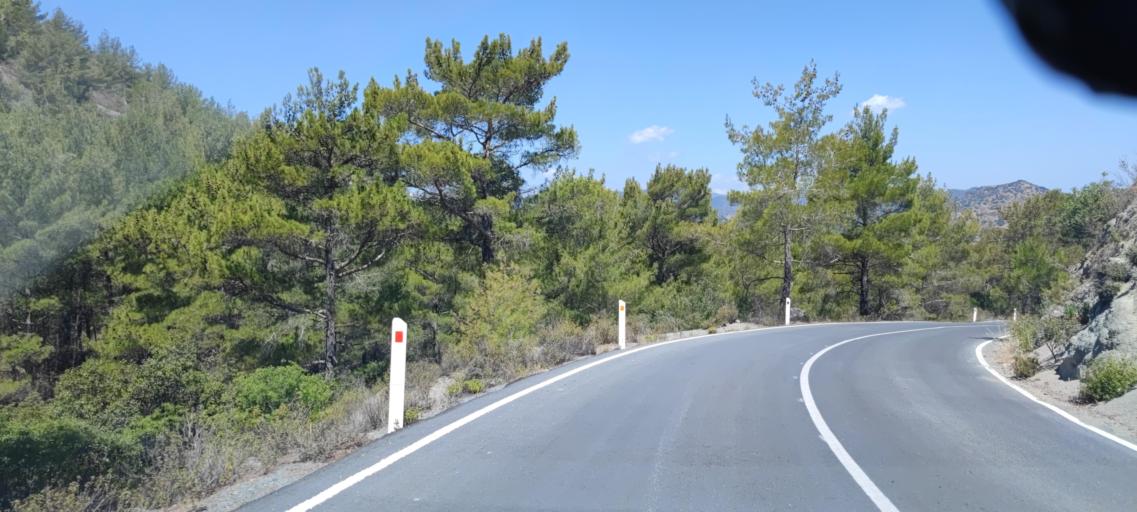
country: CY
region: Lefkosia
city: Kakopetria
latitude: 34.9189
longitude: 32.8120
